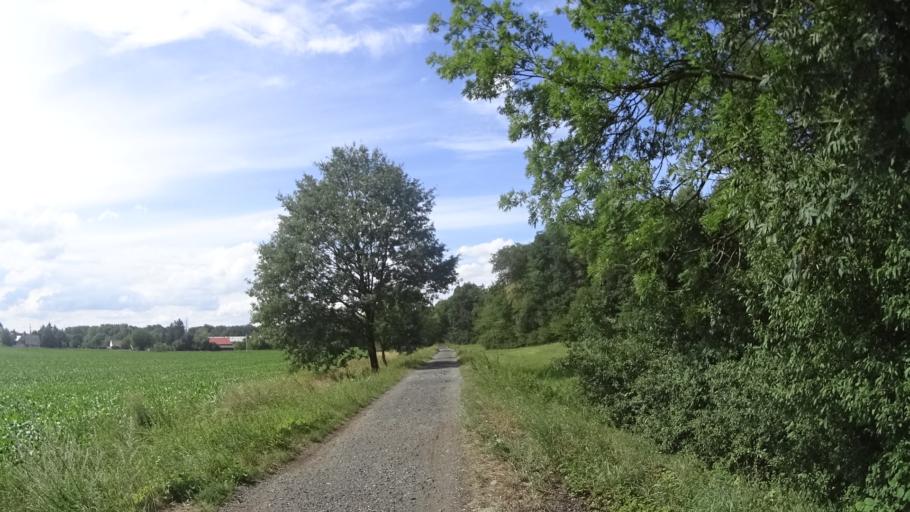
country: CZ
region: Olomoucky
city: Naklo
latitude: 49.6766
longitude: 17.1506
